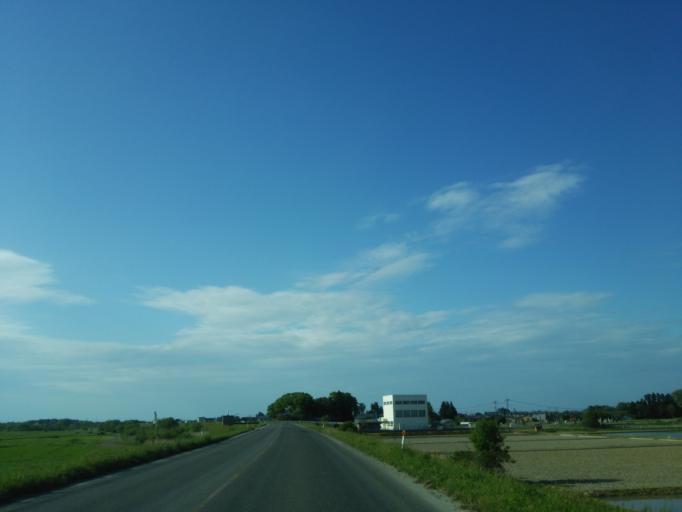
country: JP
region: Niigata
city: Niitsu-honcho
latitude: 37.7976
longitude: 139.1843
